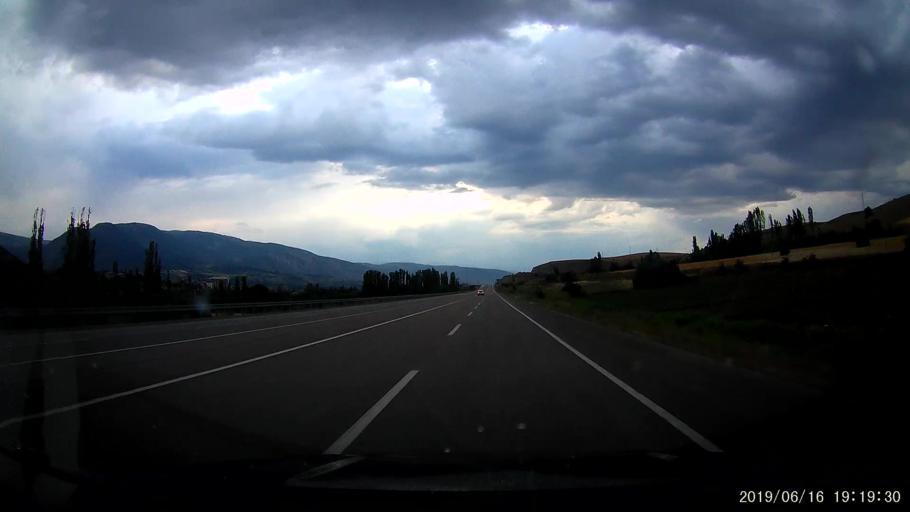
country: TR
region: Sivas
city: Akincilar
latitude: 40.0945
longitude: 38.4276
